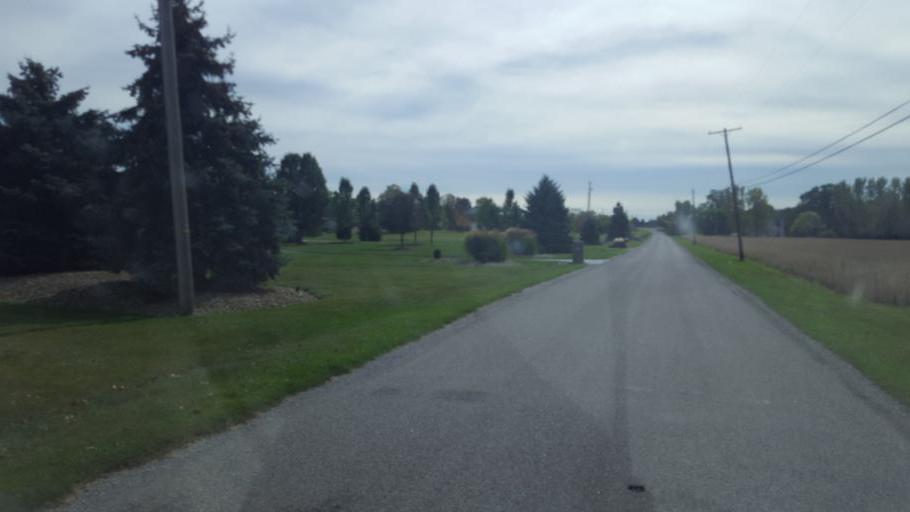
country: US
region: Ohio
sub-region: Lorain County
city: Vermilion-on-the-Lake
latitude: 41.3790
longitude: -82.3300
